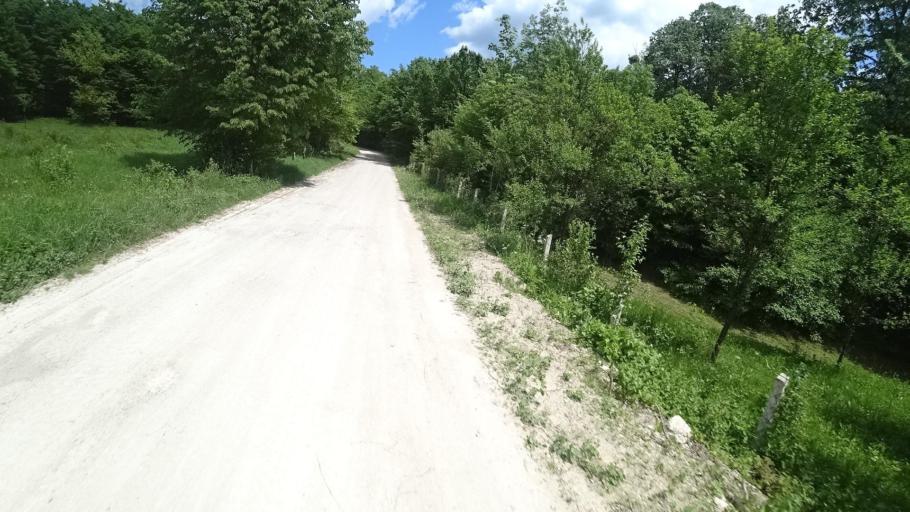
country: BA
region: Federation of Bosnia and Herzegovina
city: Ostrozac
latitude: 44.8286
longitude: 15.9687
